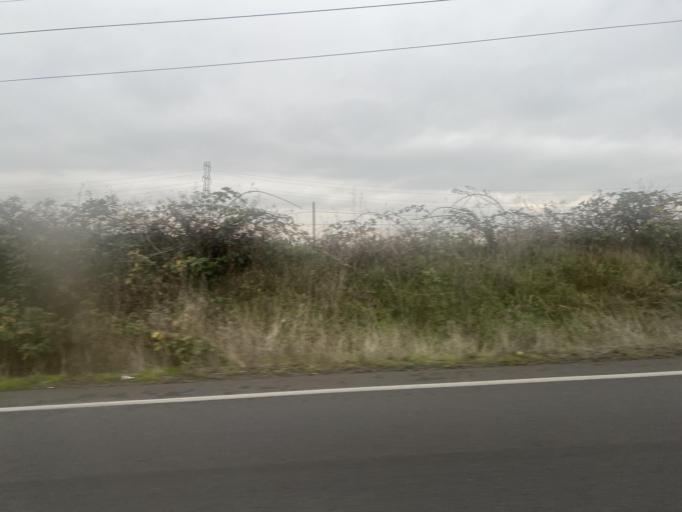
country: US
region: Oregon
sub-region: Clackamas County
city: Stafford
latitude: 45.3364
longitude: -122.7514
